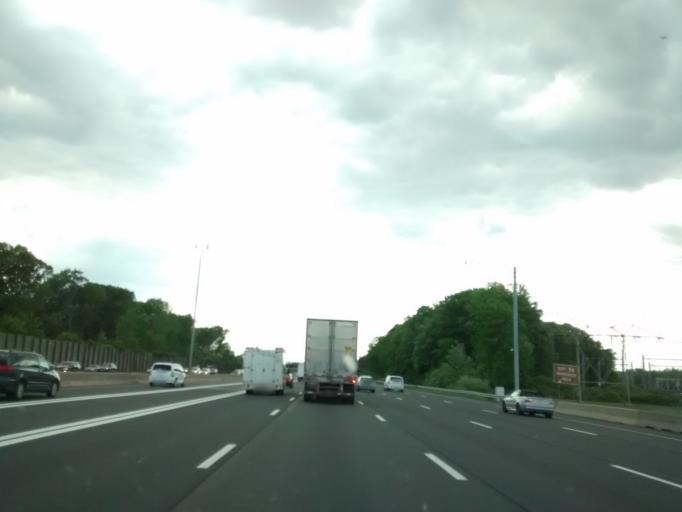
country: US
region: Connecticut
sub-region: Hartford County
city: East Hartford
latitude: 41.7690
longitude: -72.6135
